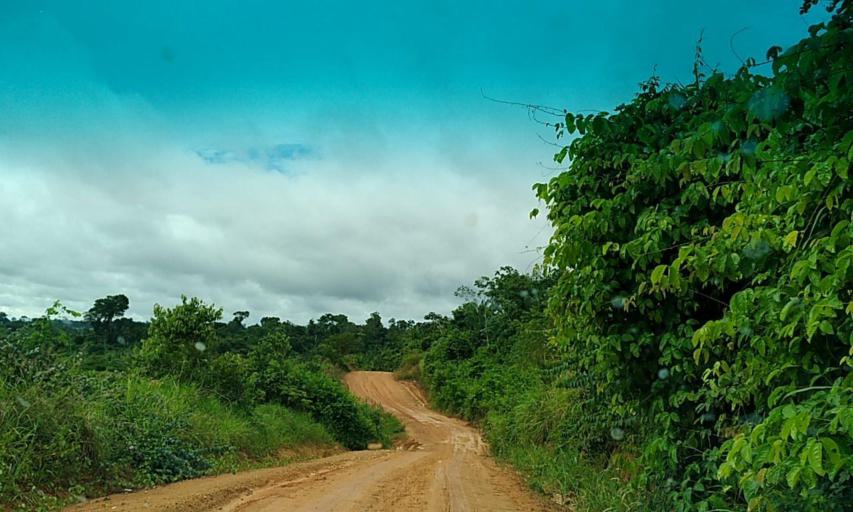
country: BR
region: Para
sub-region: Altamira
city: Altamira
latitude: -3.0933
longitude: -51.6945
